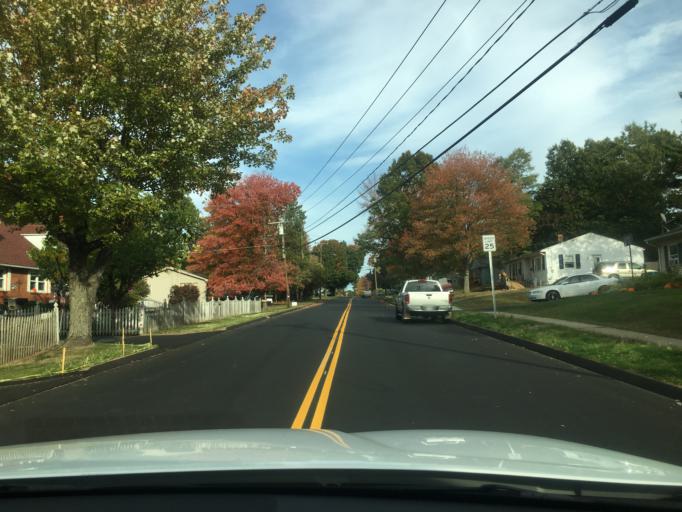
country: US
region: Connecticut
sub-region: Hartford County
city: Sherwood Manor
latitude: 42.0246
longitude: -72.5684
